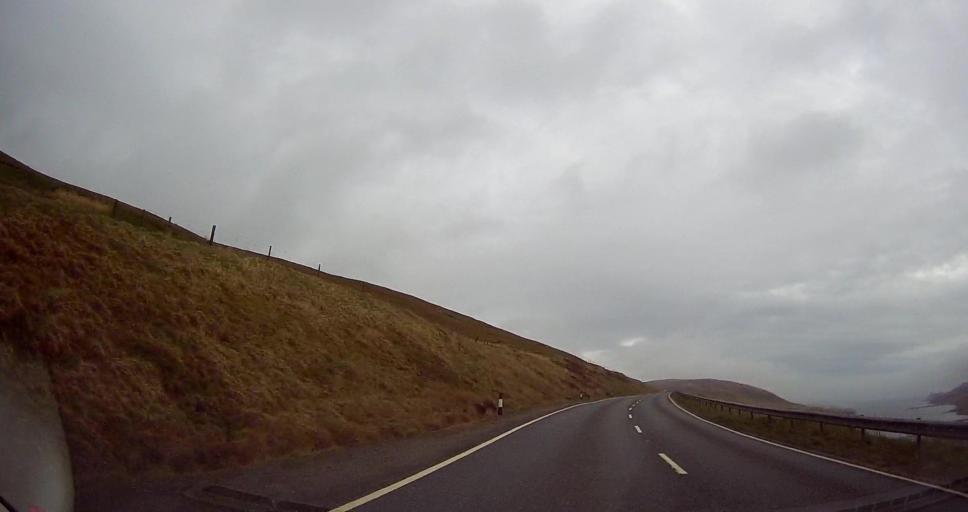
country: GB
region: Scotland
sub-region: Shetland Islands
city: Lerwick
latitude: 60.1671
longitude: -1.2277
